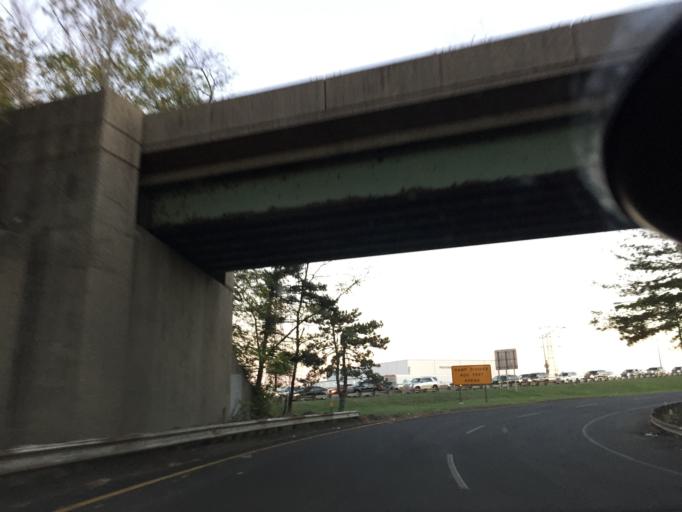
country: US
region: New Jersey
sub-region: Union County
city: Elizabeth
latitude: 40.6402
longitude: -74.2079
